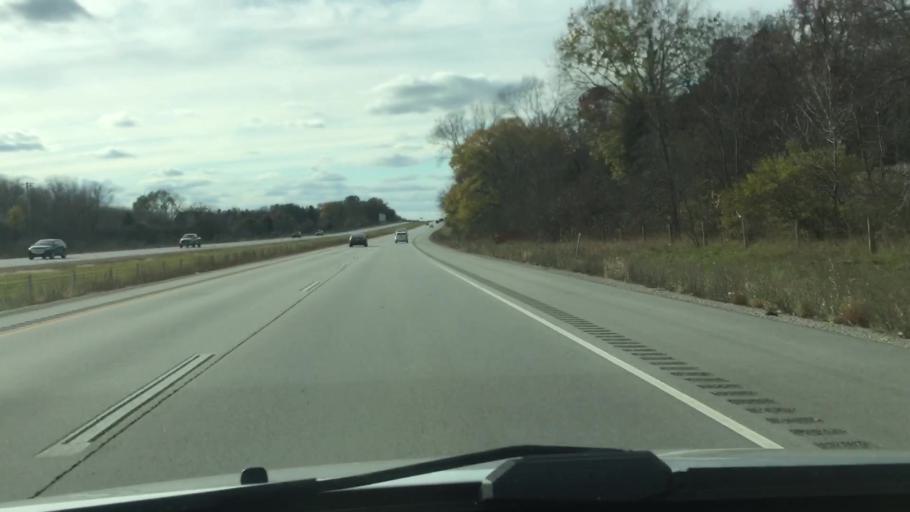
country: US
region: Wisconsin
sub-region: Waukesha County
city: Nashotah
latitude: 43.1025
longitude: -88.3847
